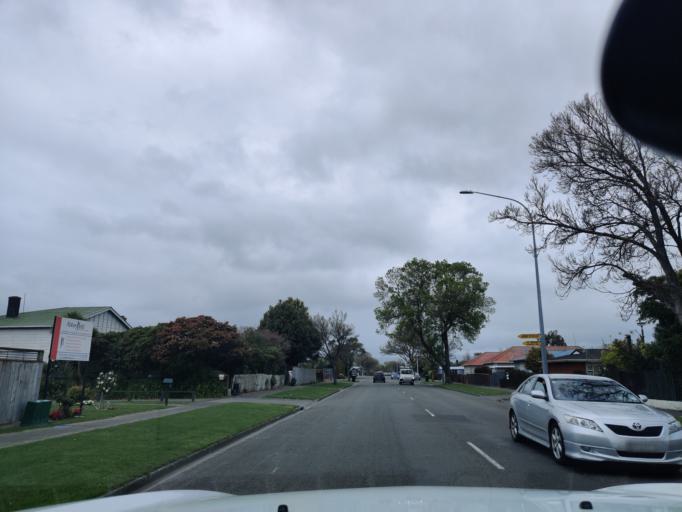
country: NZ
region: Manawatu-Wanganui
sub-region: Palmerston North City
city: Palmerston North
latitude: -40.3351
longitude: 175.6337
